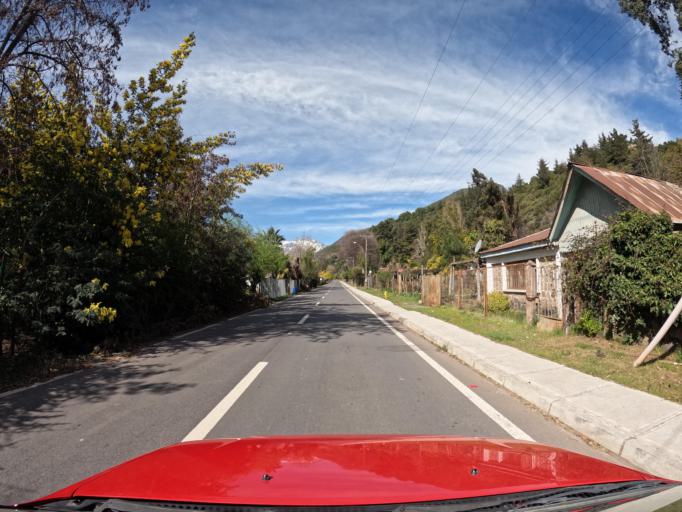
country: CL
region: O'Higgins
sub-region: Provincia de Colchagua
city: Chimbarongo
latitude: -34.9997
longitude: -70.8091
